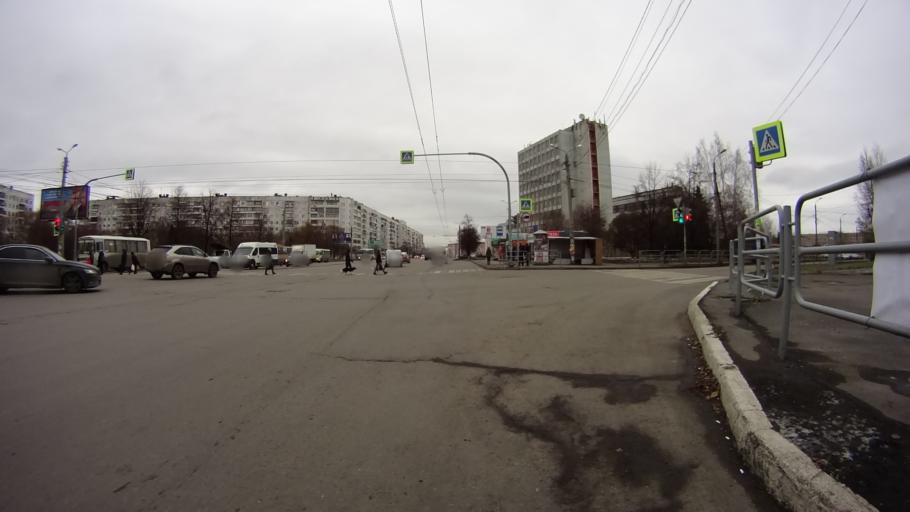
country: RU
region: Chelyabinsk
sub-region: Gorod Chelyabinsk
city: Chelyabinsk
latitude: 55.1943
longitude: 61.3538
